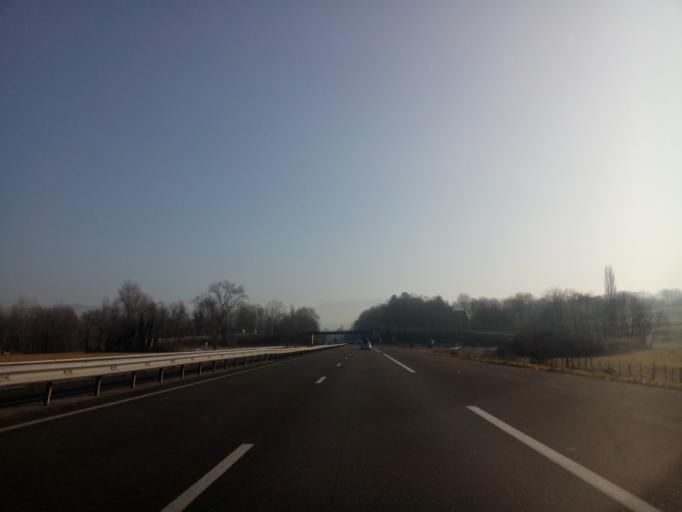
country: FR
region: Rhone-Alpes
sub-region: Departement de l'Isere
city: Romagnieu
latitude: 45.5762
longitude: 5.6384
